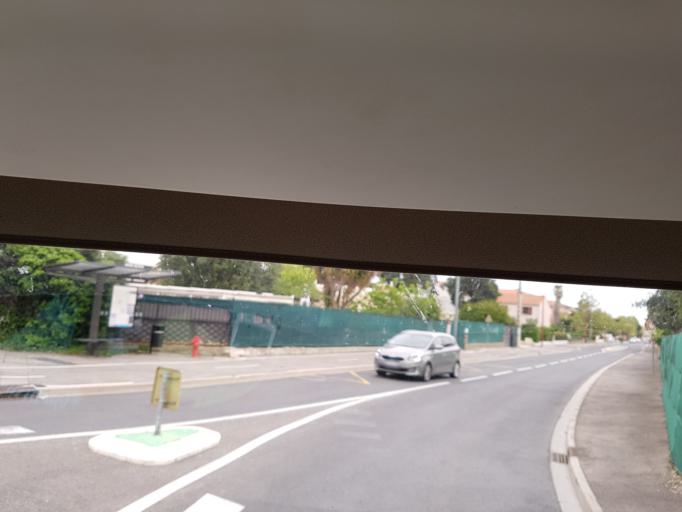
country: FR
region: Languedoc-Roussillon
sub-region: Departement des Pyrenees-Orientales
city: Saint-Esteve
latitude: 42.7068
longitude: 2.8392
